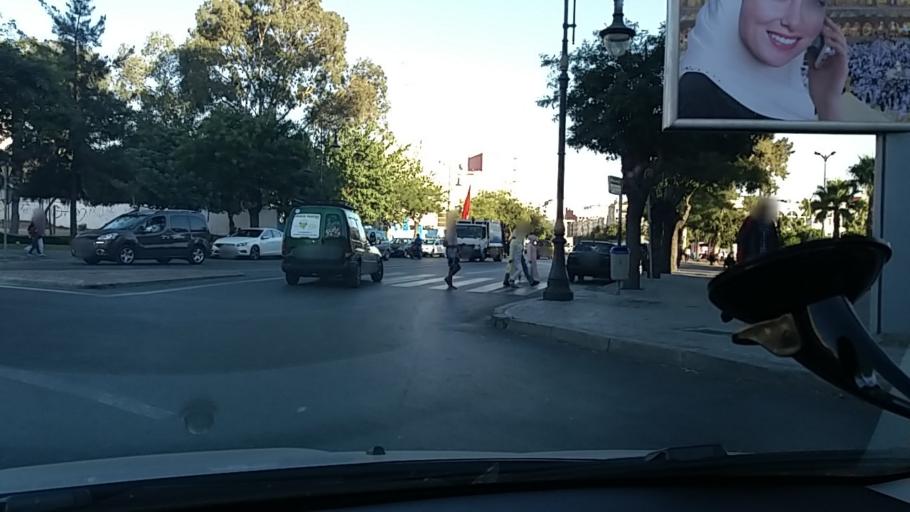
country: MA
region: Tanger-Tetouan
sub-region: Tanger-Assilah
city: Tangier
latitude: 35.7771
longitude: -5.8194
